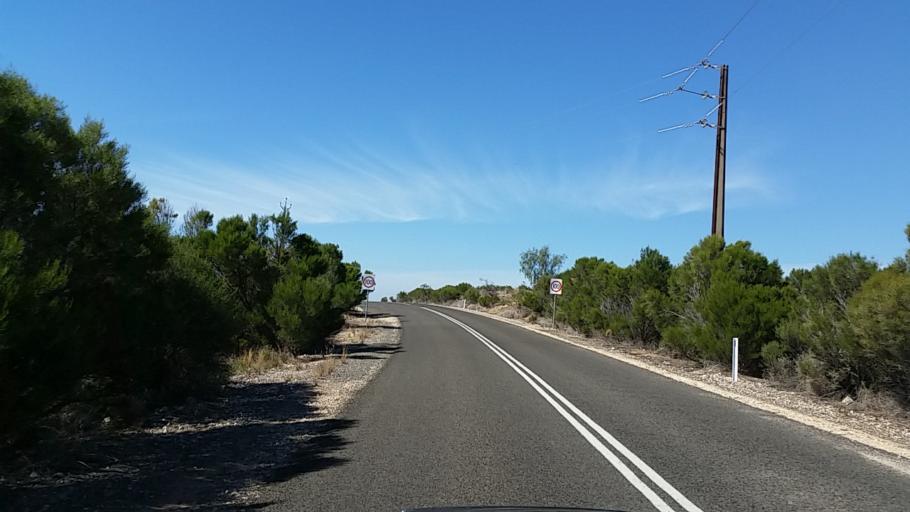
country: AU
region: South Australia
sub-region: Mid Murray
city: Mannum
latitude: -34.7458
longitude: 139.5414
